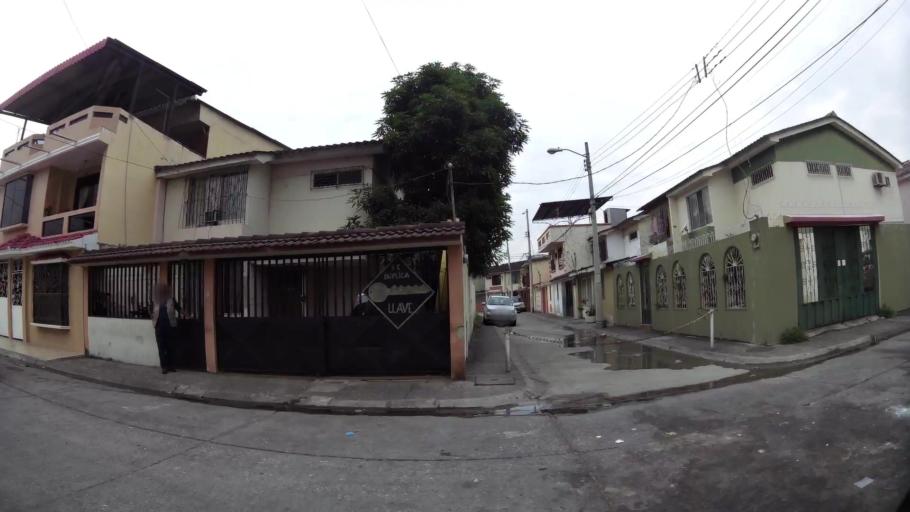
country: EC
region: Guayas
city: Eloy Alfaro
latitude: -2.1410
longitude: -79.8850
